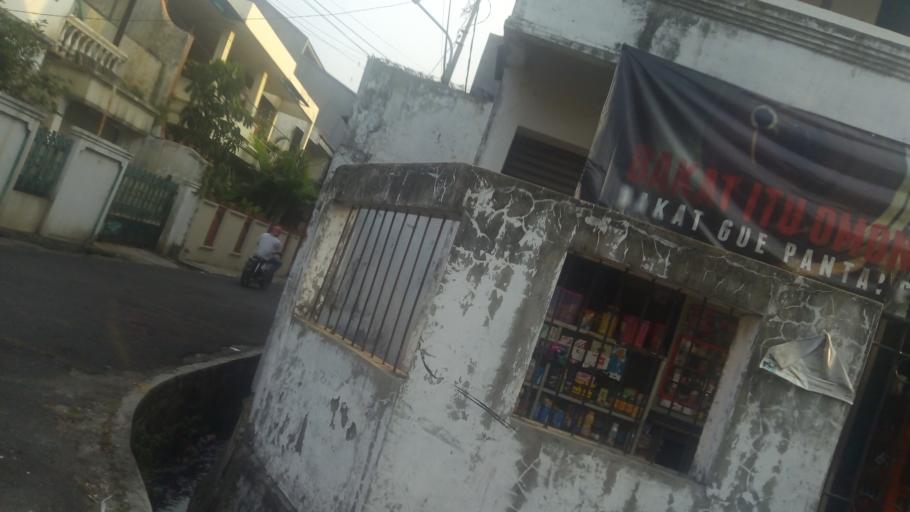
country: ID
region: Jakarta Raya
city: Jakarta
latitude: -6.2037
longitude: 106.8551
